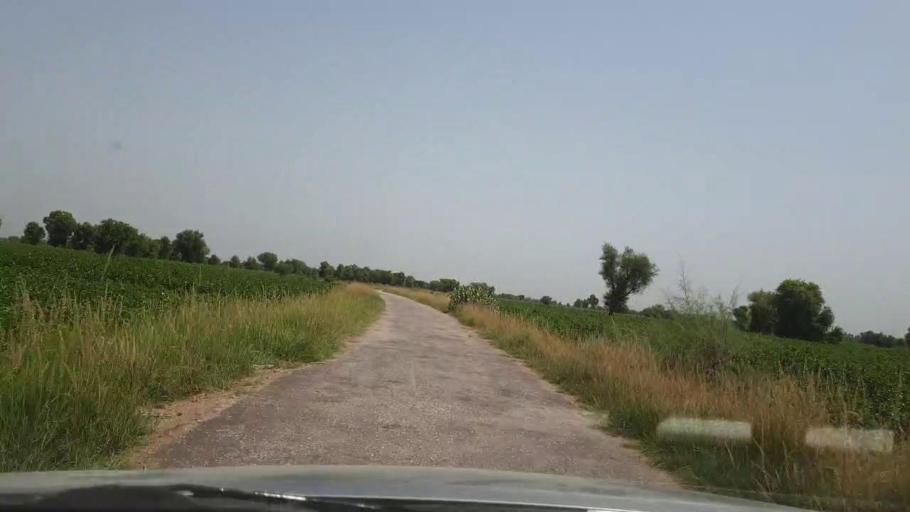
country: PK
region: Sindh
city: Pano Aqil
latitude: 27.8038
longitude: 69.2406
